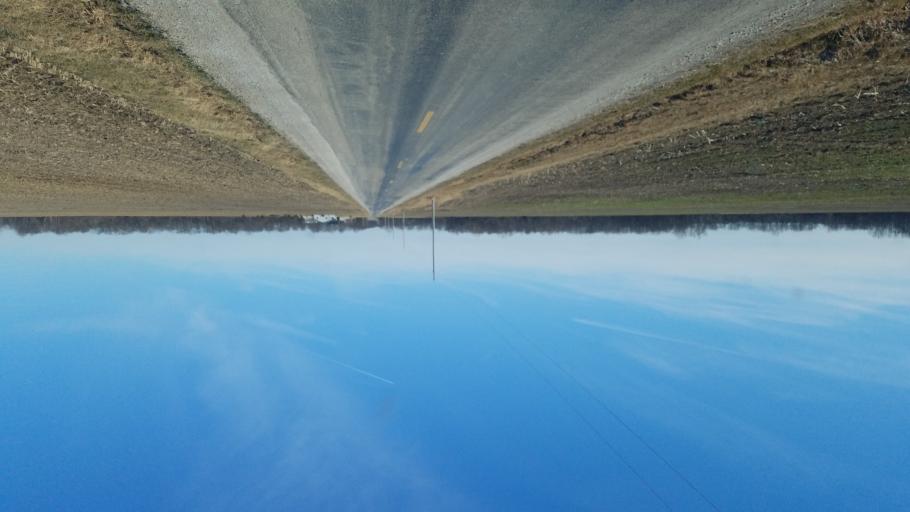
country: US
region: Ohio
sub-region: Union County
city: Richwood
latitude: 40.5263
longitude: -83.3275
